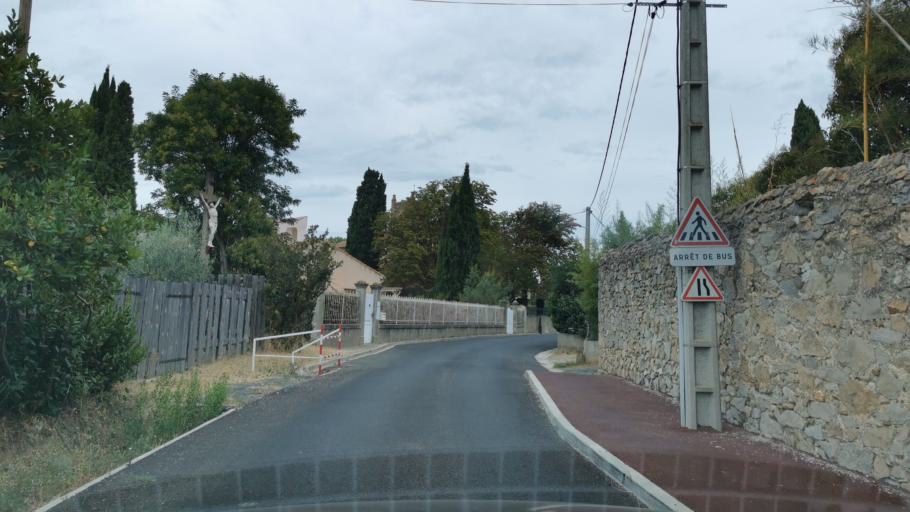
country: FR
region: Languedoc-Roussillon
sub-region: Departement de l'Aude
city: Ginestas
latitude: 43.2825
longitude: 2.8966
